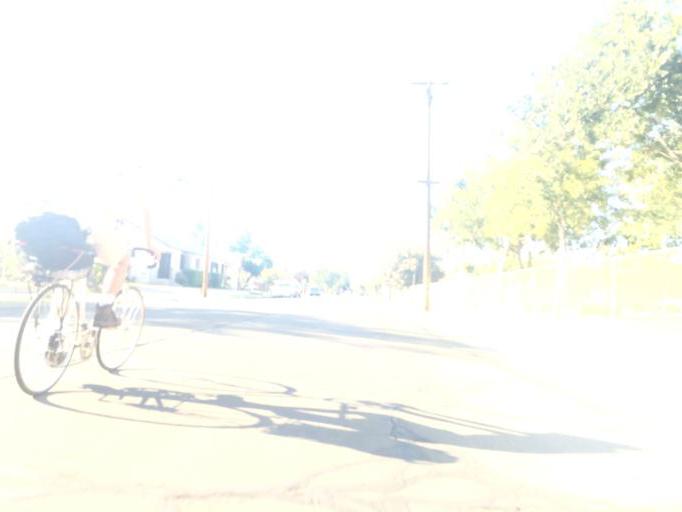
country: US
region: California
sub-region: Fresno County
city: Fresno
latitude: 36.7460
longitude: -119.7676
